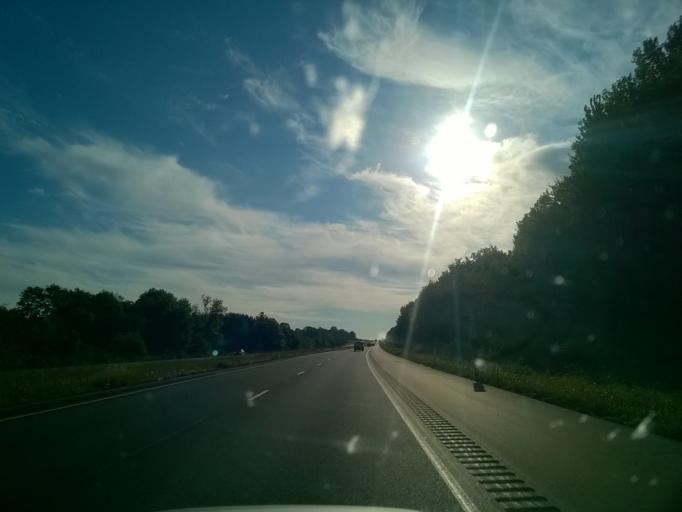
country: US
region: Indiana
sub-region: Gibson County
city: Oakland City
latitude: 38.1923
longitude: -87.3348
